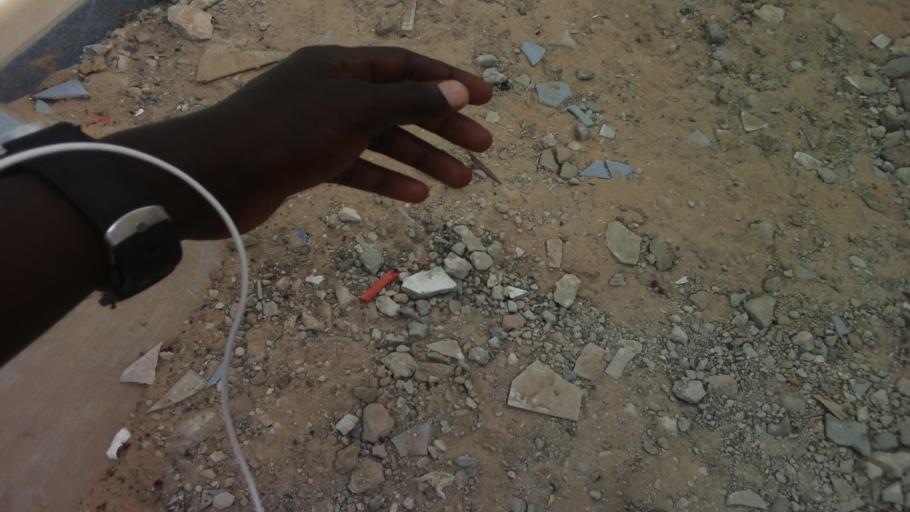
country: SN
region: Dakar
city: Pikine
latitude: 14.8018
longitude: -17.3373
